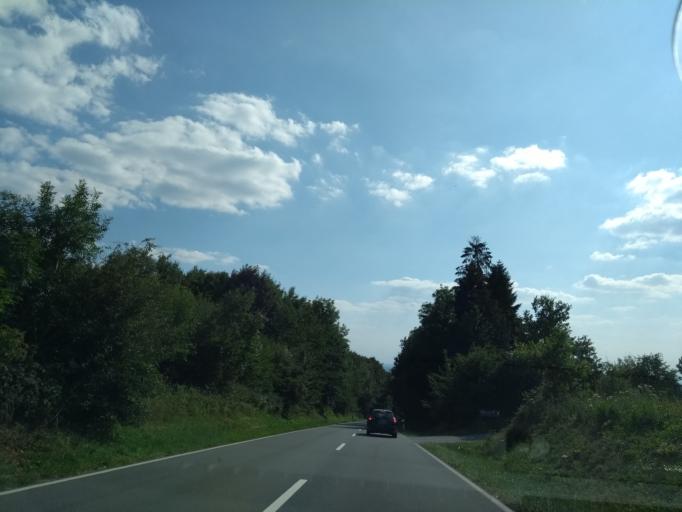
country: DE
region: North Rhine-Westphalia
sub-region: Regierungsbezirk Detmold
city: Altenbeken
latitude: 51.8148
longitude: 8.9083
